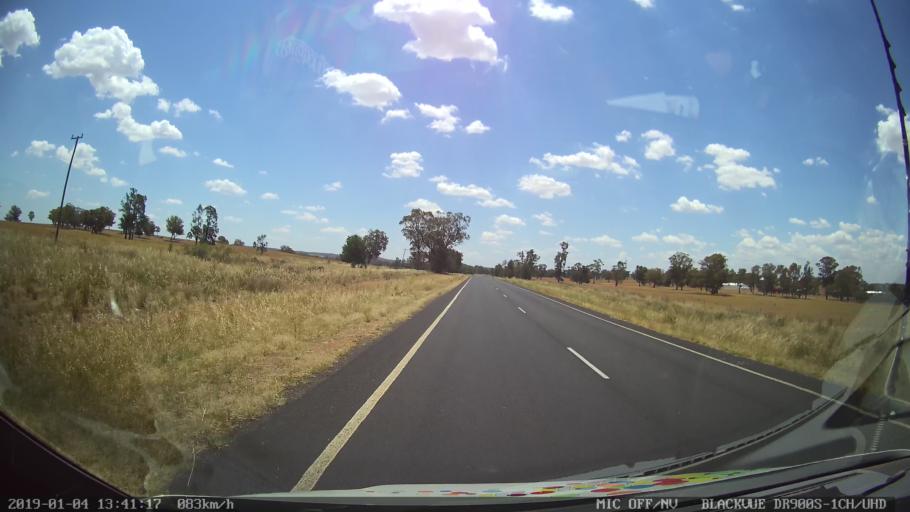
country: AU
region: New South Wales
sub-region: Dubbo Municipality
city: Dubbo
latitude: -32.5042
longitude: 148.5537
